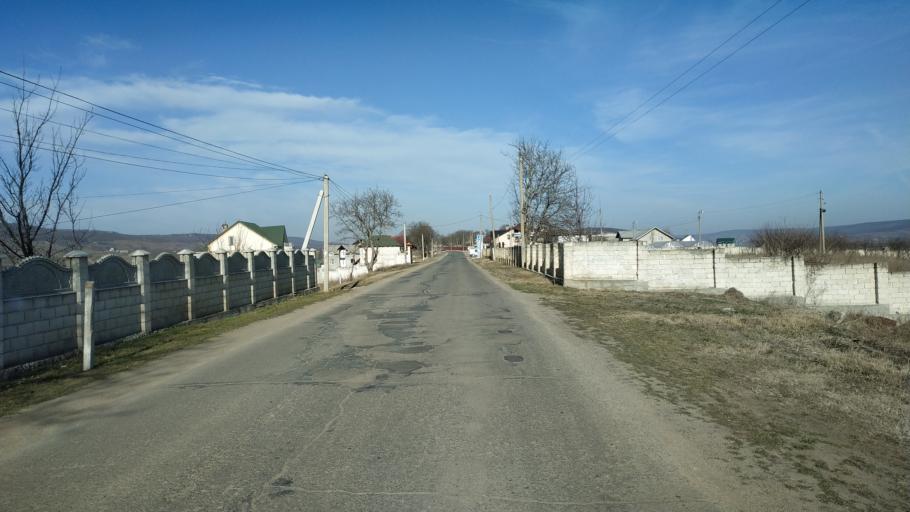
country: MD
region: Chisinau
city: Vatra
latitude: 47.0184
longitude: 28.6514
